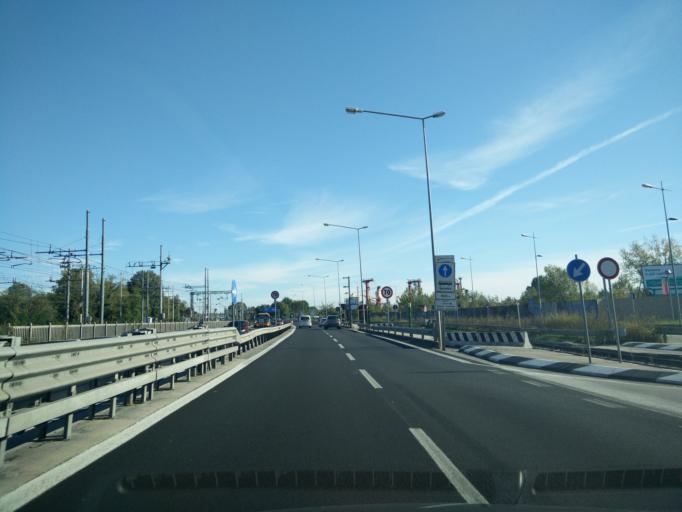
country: IT
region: Veneto
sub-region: Provincia di Venezia
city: Mestre
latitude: 45.4713
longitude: 12.2581
